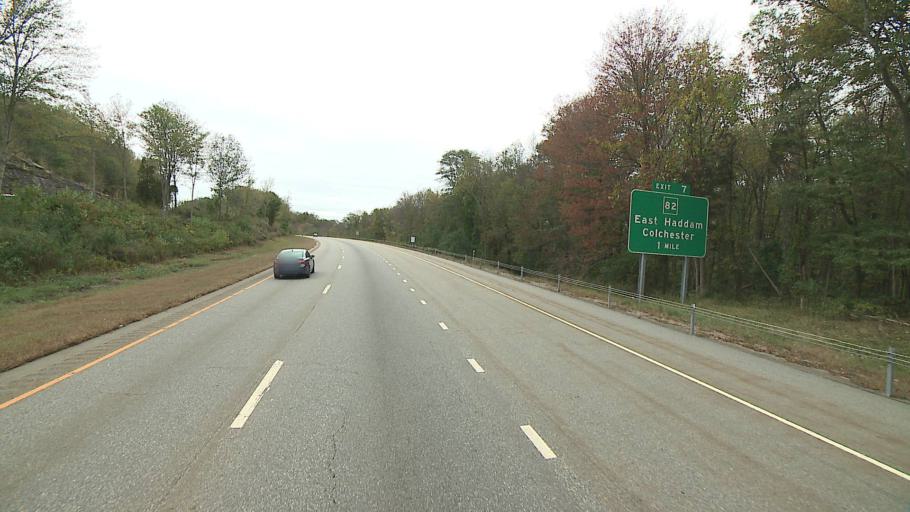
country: US
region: Connecticut
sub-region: Middlesex County
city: Chester Center
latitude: 41.4077
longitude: -72.4762
